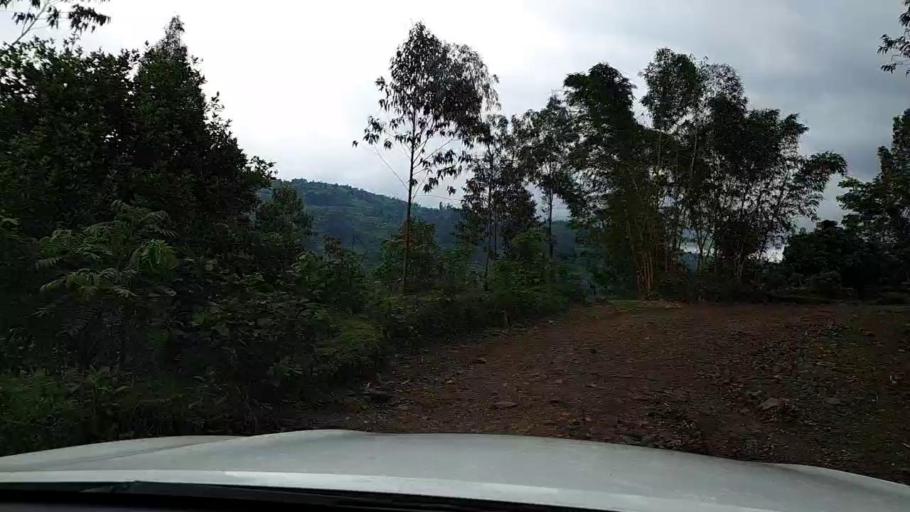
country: RW
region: Western Province
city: Cyangugu
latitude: -2.5573
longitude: 29.0357
